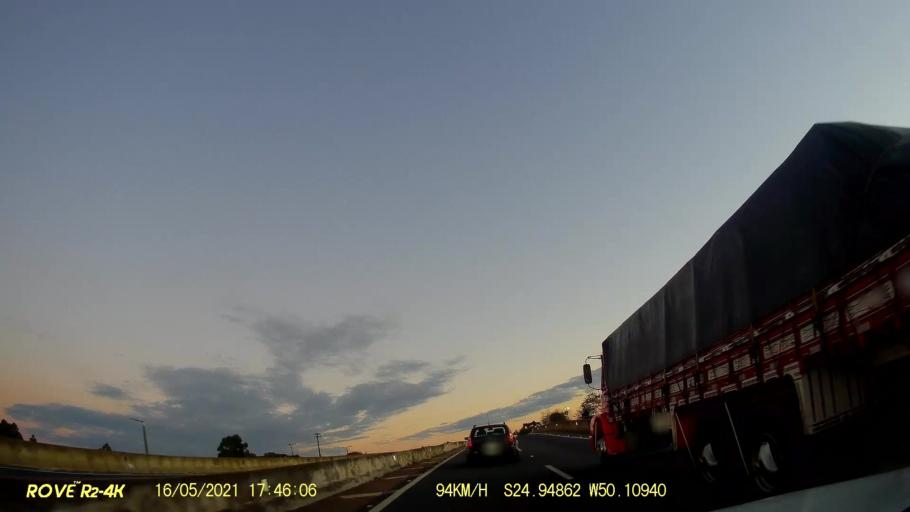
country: BR
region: Parana
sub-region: Carambei
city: Carambei
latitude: -24.9486
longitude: -50.1094
